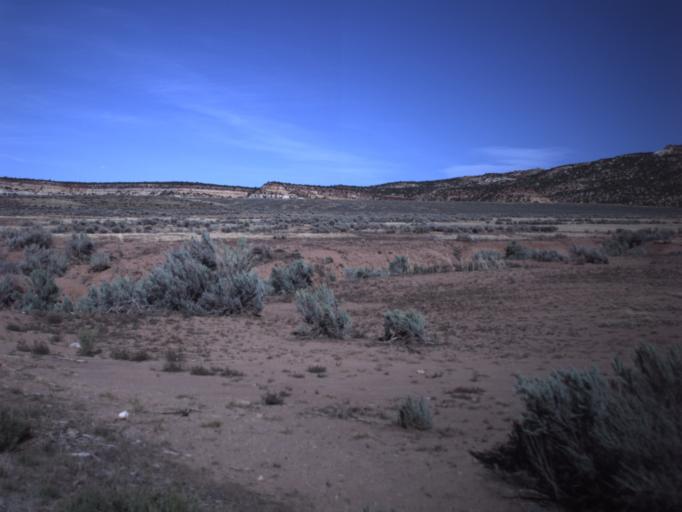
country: US
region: Utah
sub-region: San Juan County
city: Monticello
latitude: 38.0172
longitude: -109.4305
